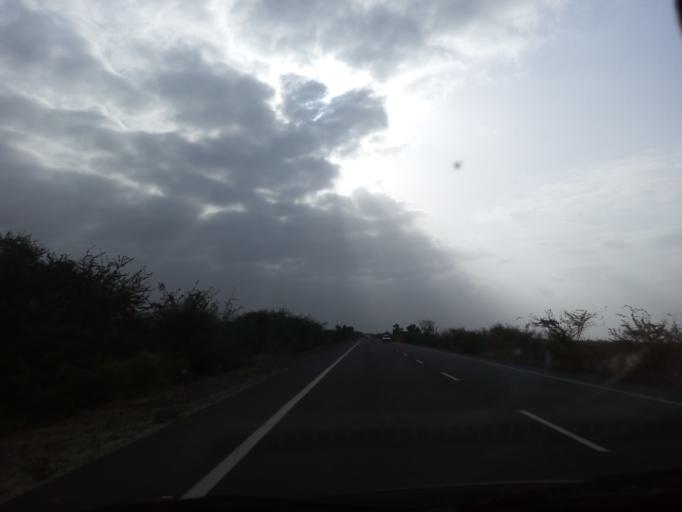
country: IN
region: Gujarat
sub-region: Kachchh
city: Anjar
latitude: 23.2891
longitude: 70.0191
